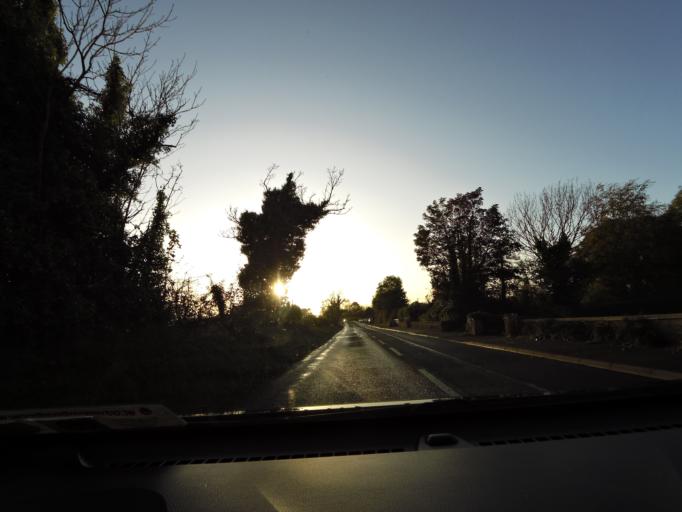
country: IE
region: Connaught
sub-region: Roscommon
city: Castlerea
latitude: 53.6772
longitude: -8.5853
